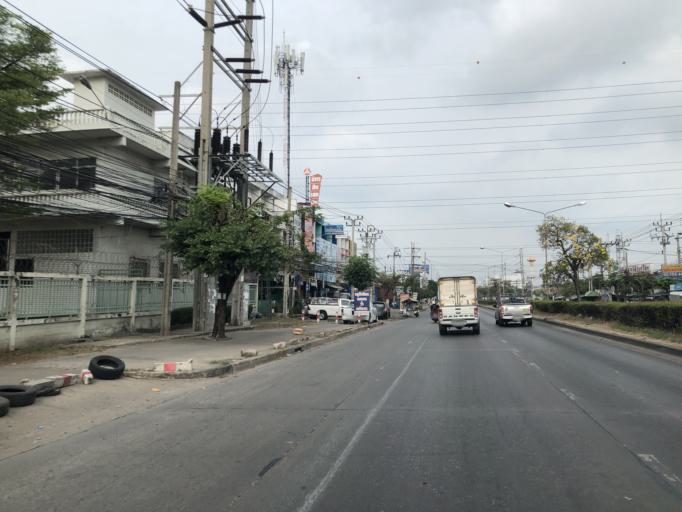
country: TH
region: Bangkok
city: Bang Na
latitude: 13.6074
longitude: 100.6858
